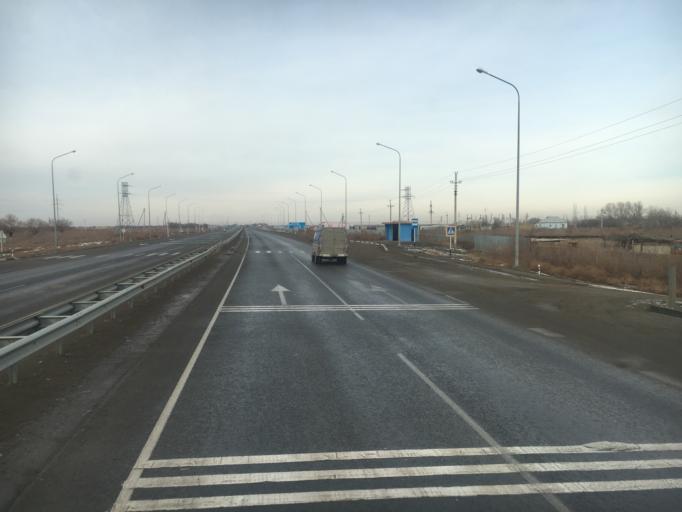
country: KZ
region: Qyzylorda
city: Shieli
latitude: 44.1382
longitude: 66.9677
